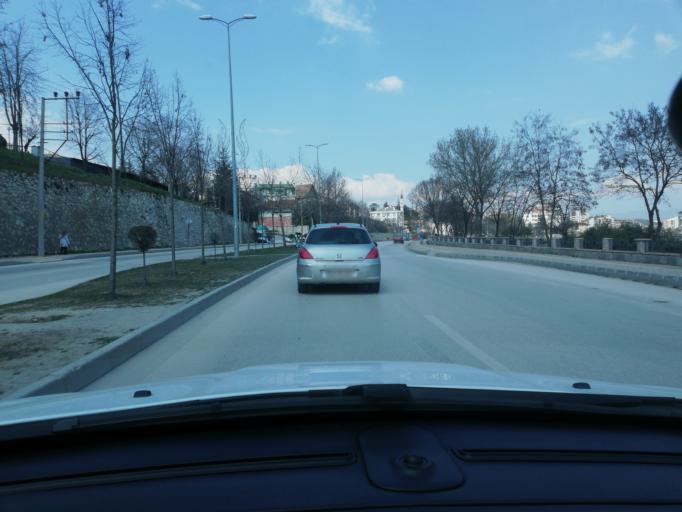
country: TR
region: Kastamonu
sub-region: Cide
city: Kastamonu
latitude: 41.3985
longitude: 33.7807
